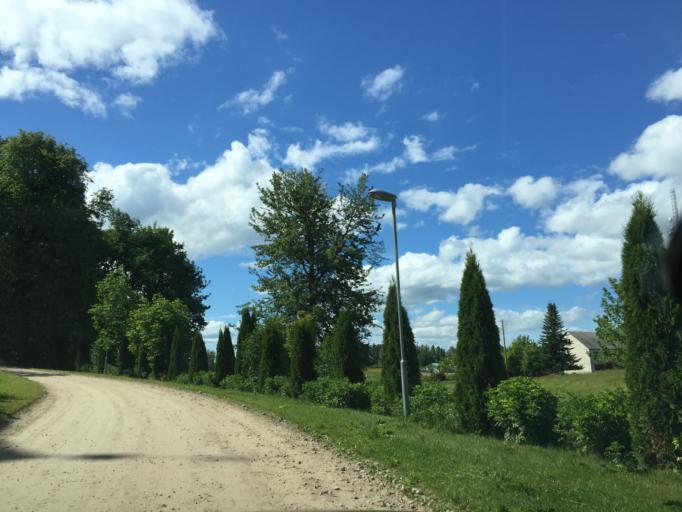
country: LT
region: Panevezys
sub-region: Birzai
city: Birzai
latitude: 56.3804
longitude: 24.6440
